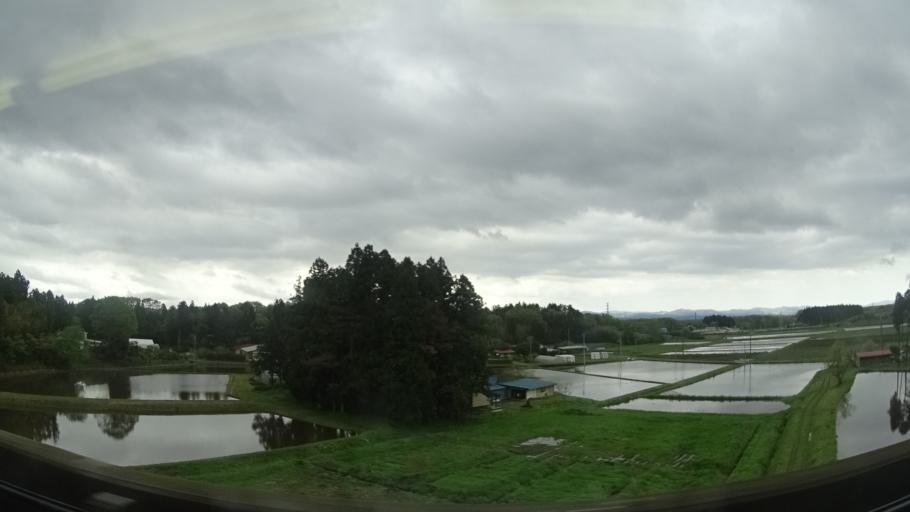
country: JP
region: Tochigi
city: Kuroiso
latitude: 37.0205
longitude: 140.1001
